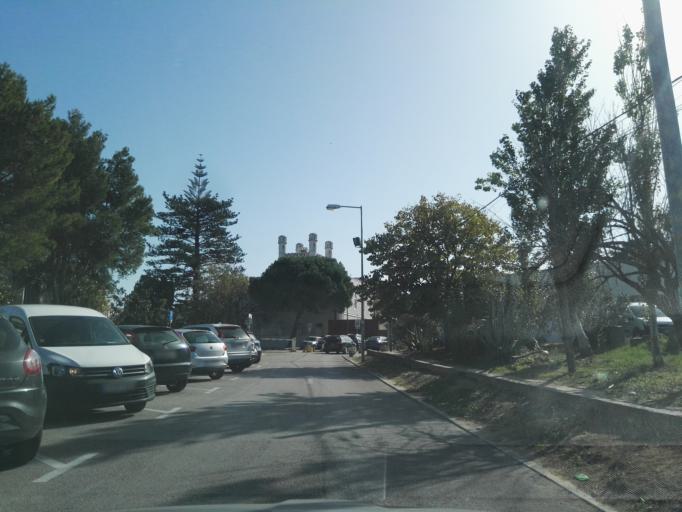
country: PT
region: Lisbon
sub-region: Lisbon
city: Lisbon
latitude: 38.7488
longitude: -9.1554
